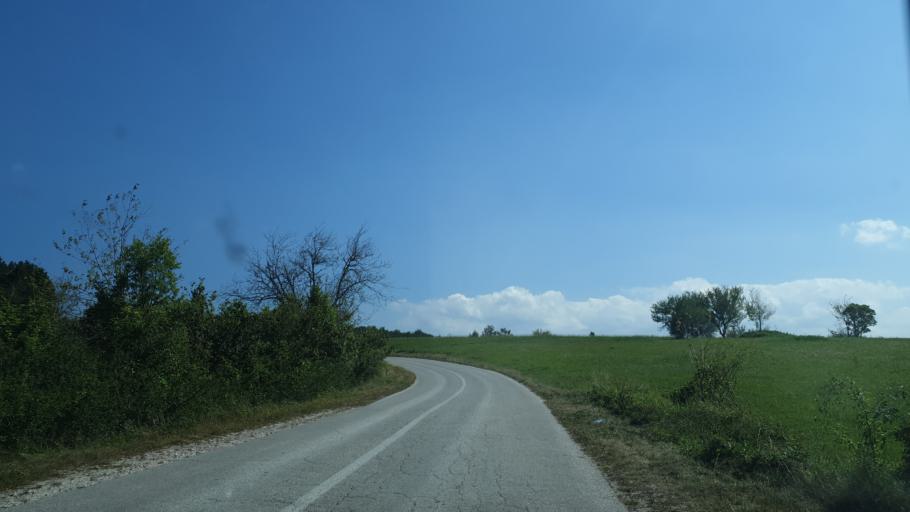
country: RS
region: Central Serbia
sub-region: Zlatiborski Okrug
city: Cajetina
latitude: 43.6749
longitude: 19.8408
